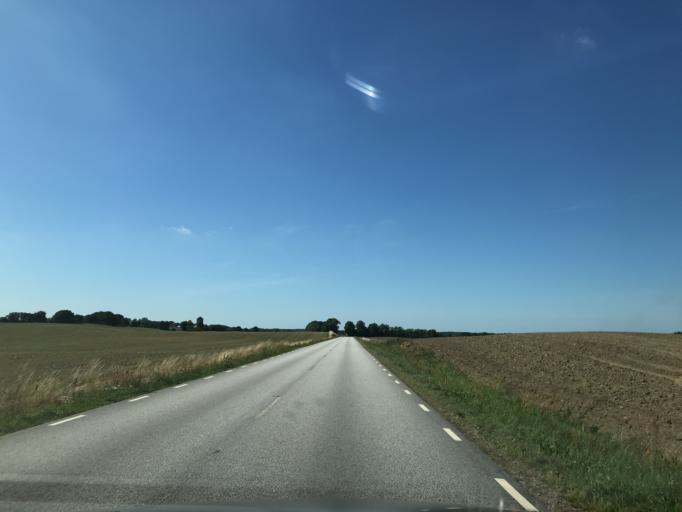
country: SE
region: Skane
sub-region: Tomelilla Kommun
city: Tomelilla
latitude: 55.6433
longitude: 13.9935
